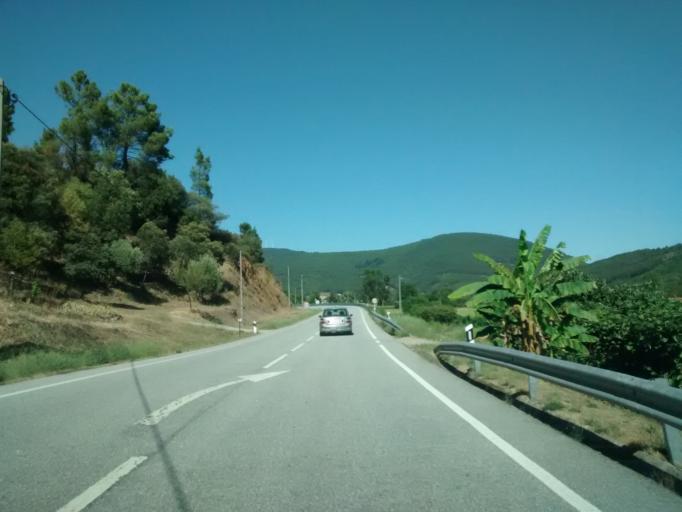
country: PT
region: Castelo Branco
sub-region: Belmonte
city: Belmonte
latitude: 40.3958
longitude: -7.4235
